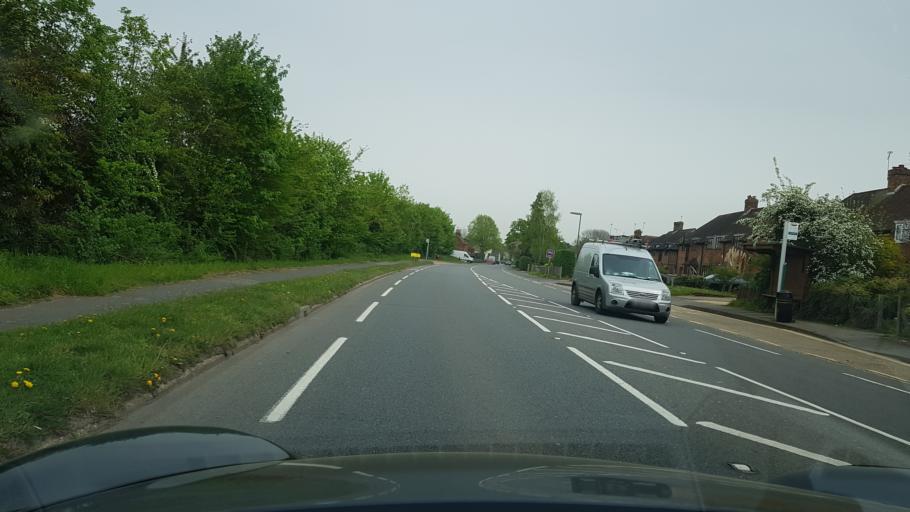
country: GB
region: England
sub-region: Surrey
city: Ripley
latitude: 51.2973
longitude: -0.4977
